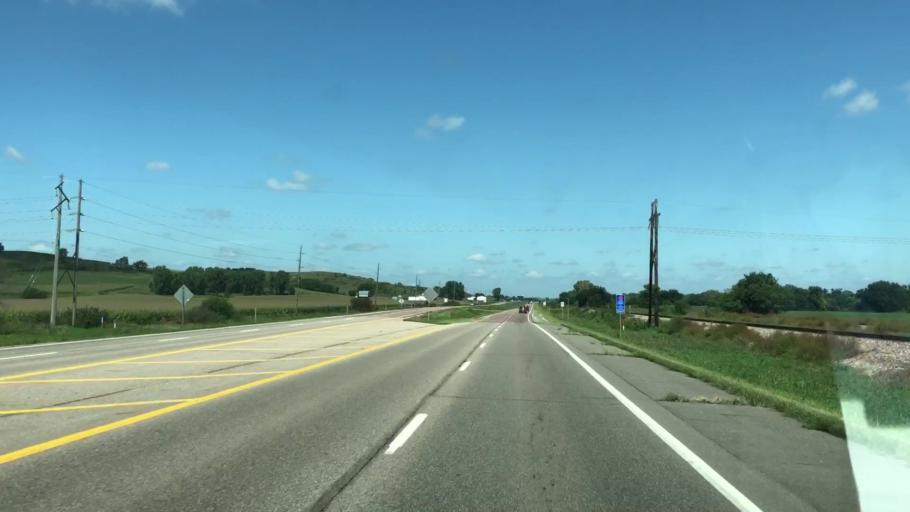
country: US
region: Iowa
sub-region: Woodbury County
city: Sioux City
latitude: 42.6329
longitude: -96.2902
